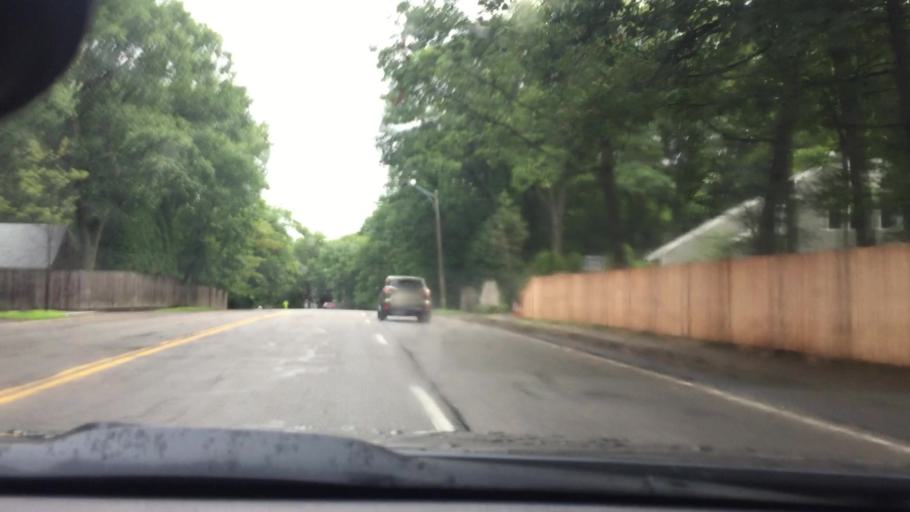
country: US
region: Massachusetts
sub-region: Suffolk County
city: Jamaica Plain
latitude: 42.3155
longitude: -71.1632
